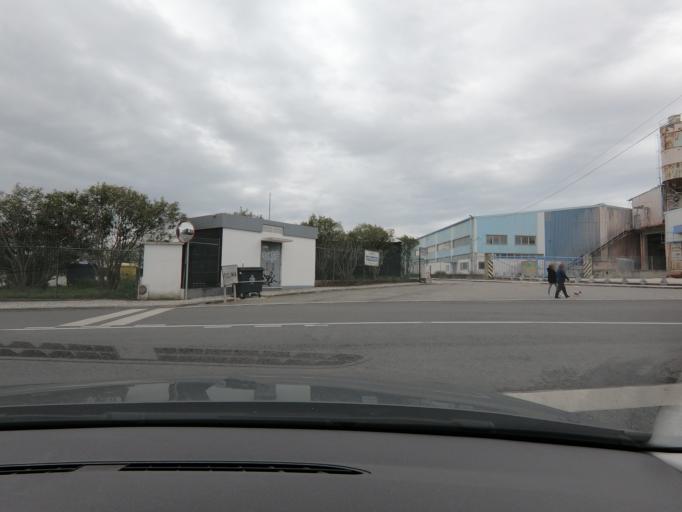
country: PT
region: Lisbon
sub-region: Cascais
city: Sao Domingos de Rana
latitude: 38.7242
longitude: -9.3283
